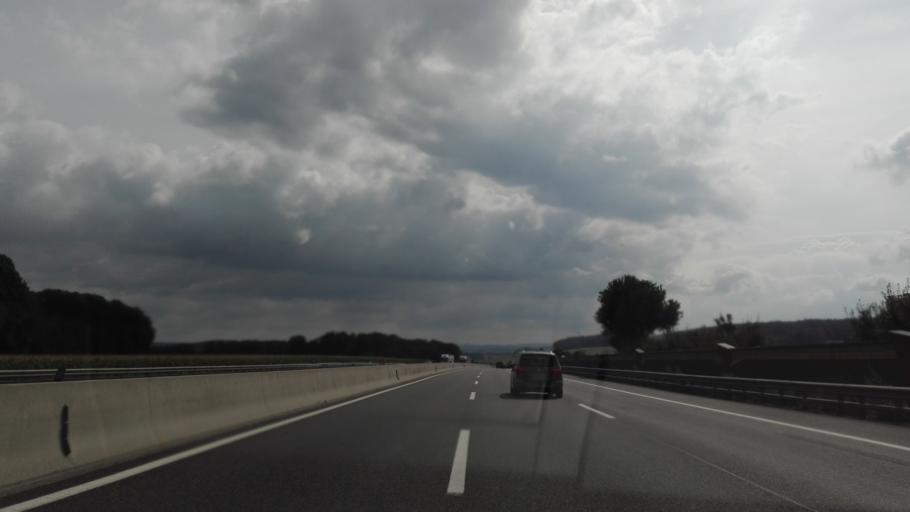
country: AT
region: Lower Austria
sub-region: Politischer Bezirk Sankt Polten
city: Pyhra
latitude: 48.1862
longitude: 15.7133
